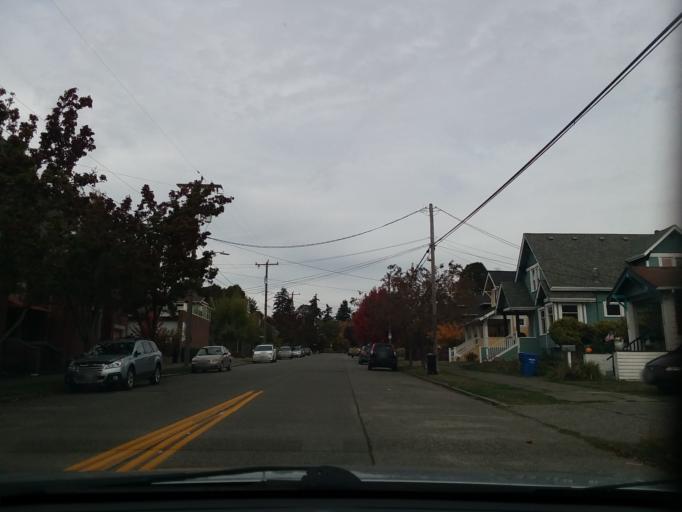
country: US
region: Washington
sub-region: King County
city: Seattle
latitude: 47.6762
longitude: -122.3821
